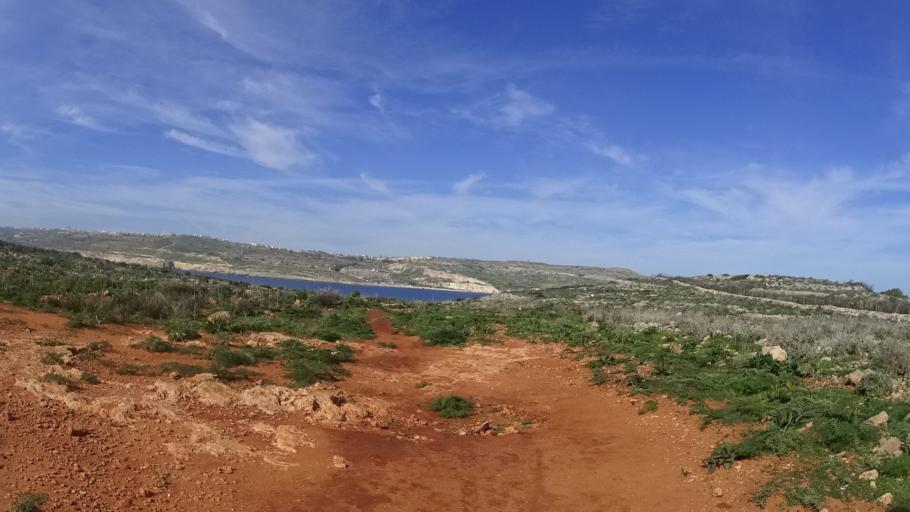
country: MT
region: Il-Qala
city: Qala
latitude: 36.0159
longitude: 14.3263
